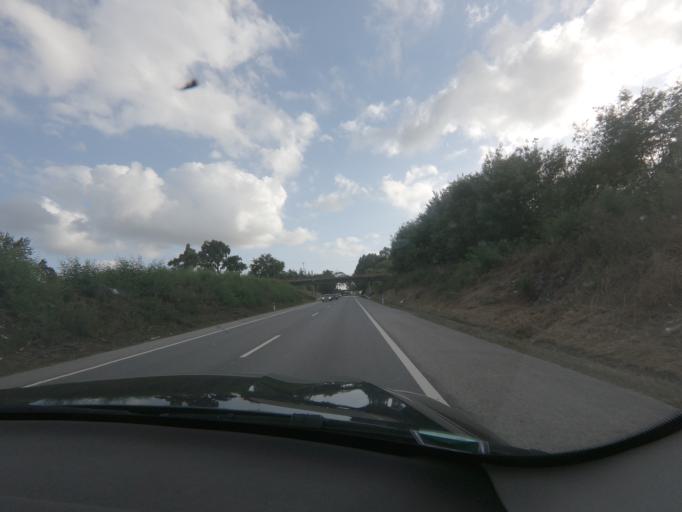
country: PT
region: Viseu
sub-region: Concelho de Tondela
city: Tondela
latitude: 40.5723
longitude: -8.0343
